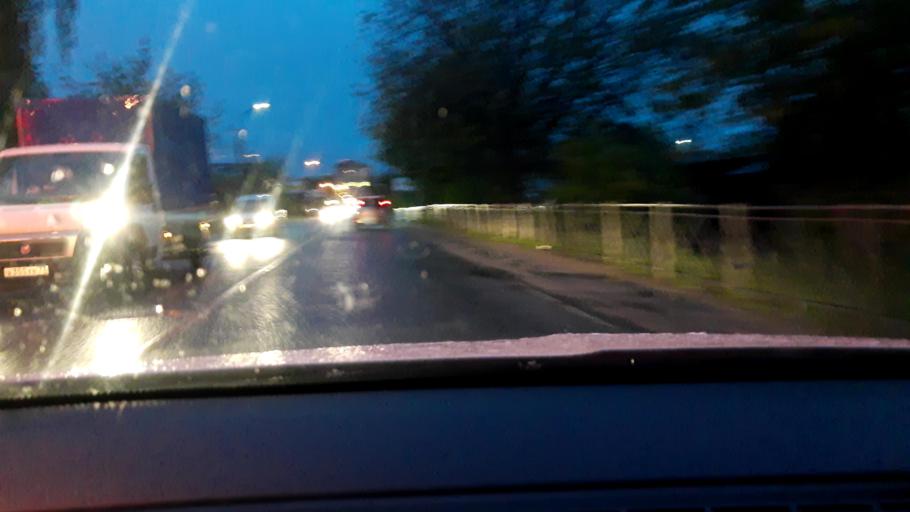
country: RU
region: Moskovskaya
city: Shchelkovo
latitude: 55.9351
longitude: 37.9773
